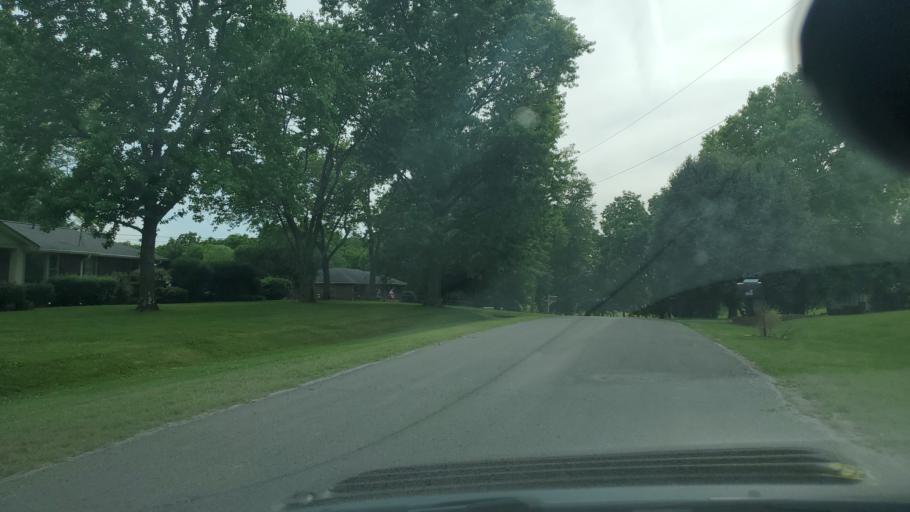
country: US
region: Tennessee
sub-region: Davidson County
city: Lakewood
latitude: 36.2209
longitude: -86.6858
